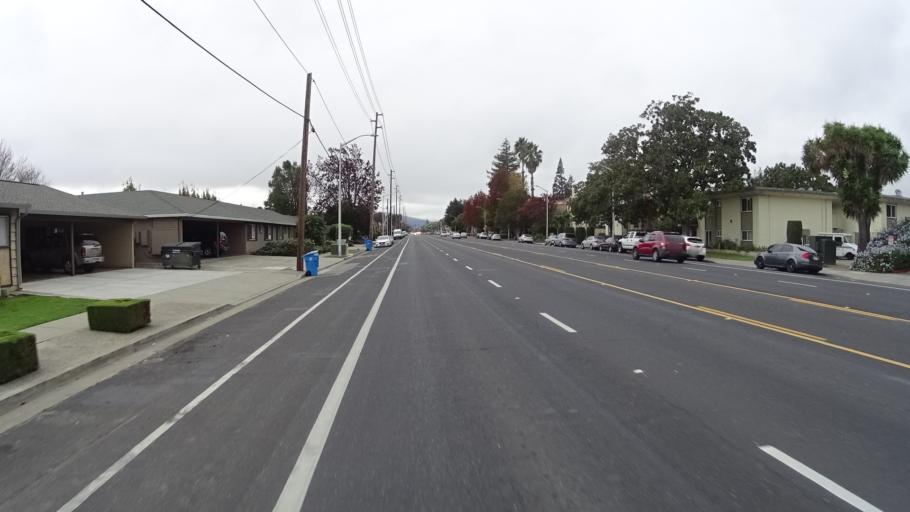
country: US
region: California
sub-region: Santa Clara County
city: Santa Clara
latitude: 37.3378
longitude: -121.9884
